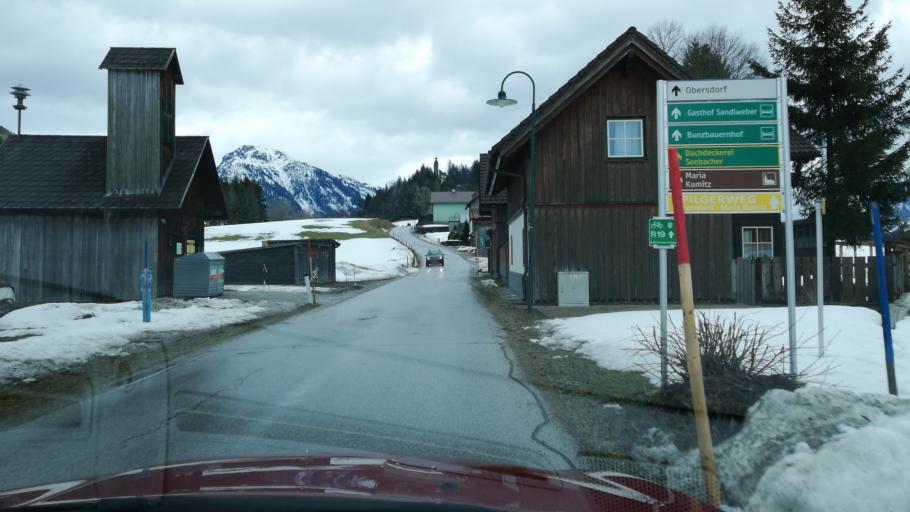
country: AT
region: Styria
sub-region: Politischer Bezirk Liezen
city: Bad Aussee
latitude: 47.5675
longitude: 13.8733
